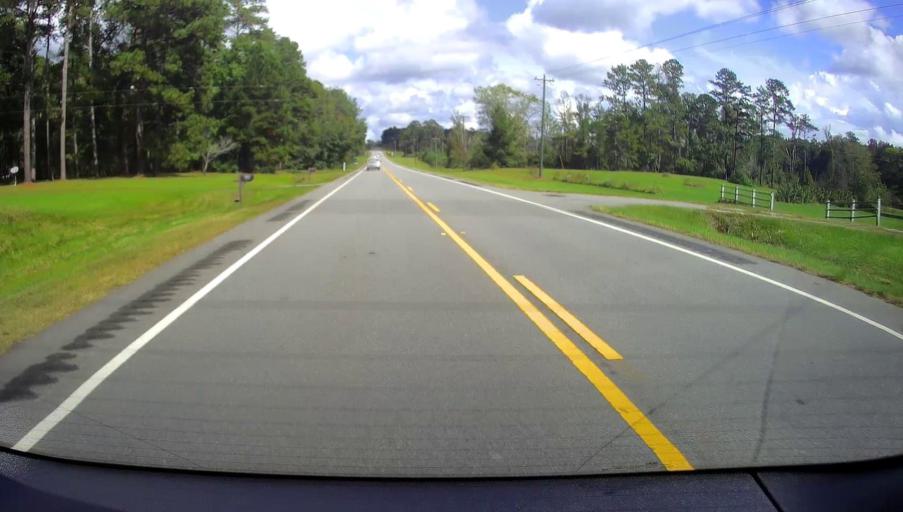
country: US
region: Georgia
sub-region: Baldwin County
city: Milledgeville
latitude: 33.0765
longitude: -83.3114
